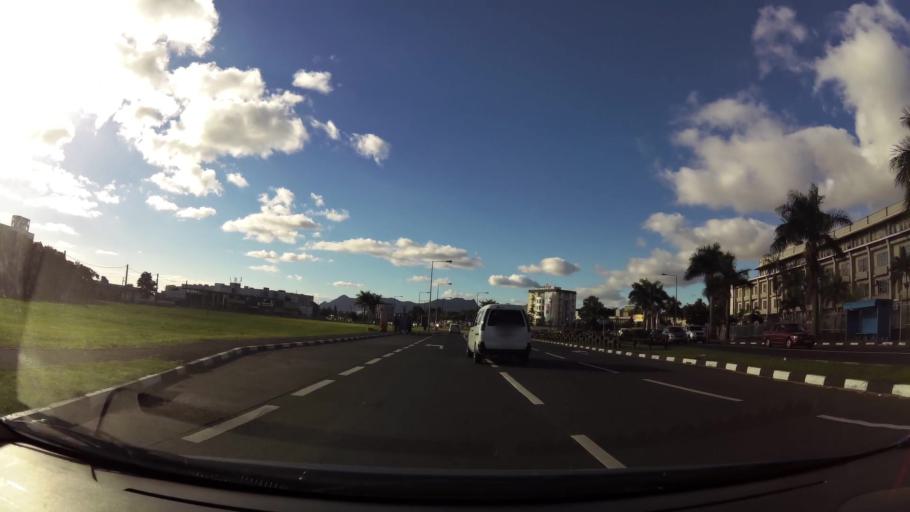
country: MU
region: Plaines Wilhems
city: Quatre Bornes
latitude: -20.2751
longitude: 57.4968
